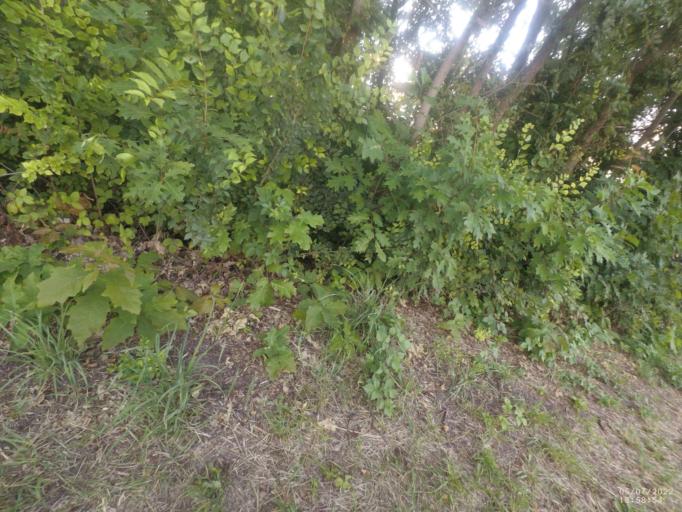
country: DE
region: Rheinland-Pfalz
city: Hassloch
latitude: 49.3484
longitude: 8.2504
